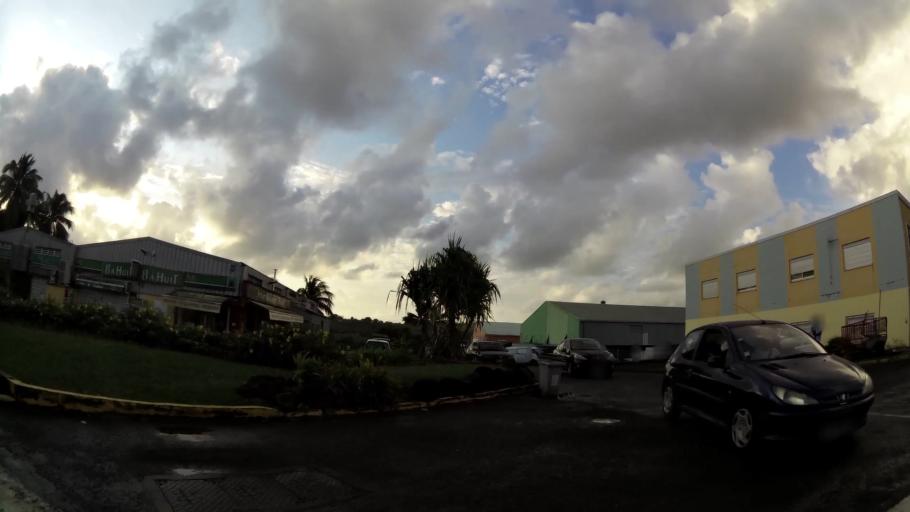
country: GP
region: Guadeloupe
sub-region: Guadeloupe
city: Petit-Bourg
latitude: 16.1334
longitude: -61.5790
